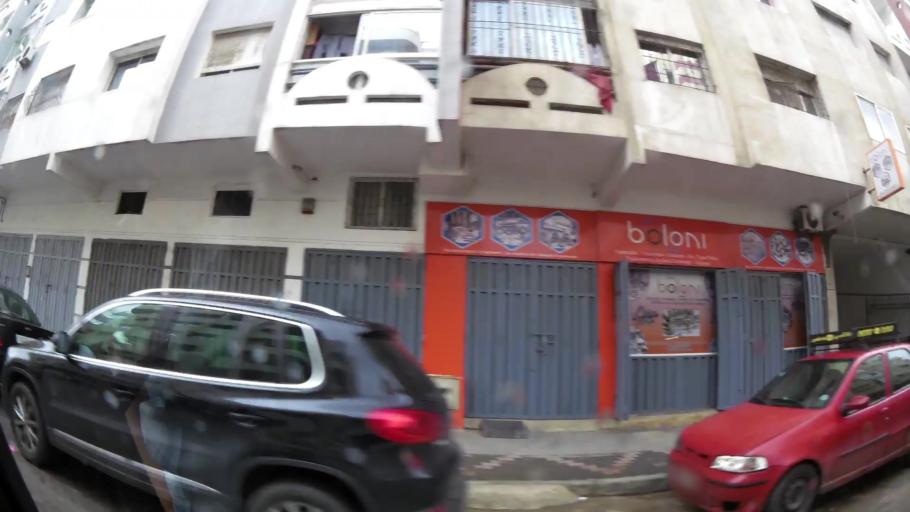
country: MA
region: Grand Casablanca
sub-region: Casablanca
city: Casablanca
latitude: 33.5819
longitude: -7.5980
